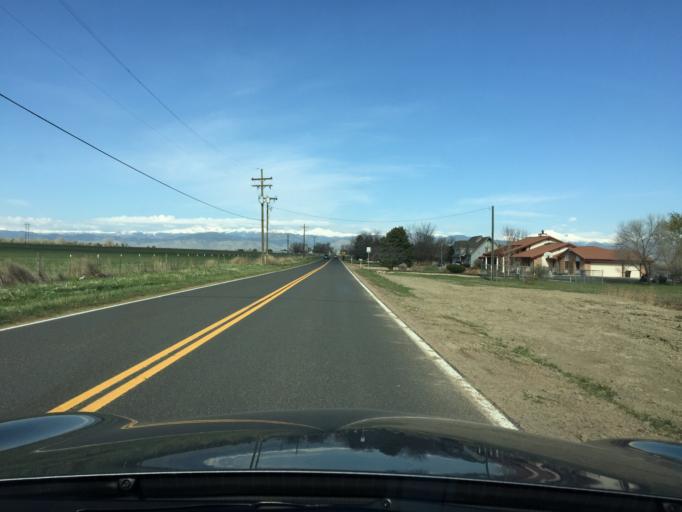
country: US
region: Colorado
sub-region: Boulder County
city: Longmont
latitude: 40.1163
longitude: -105.1059
